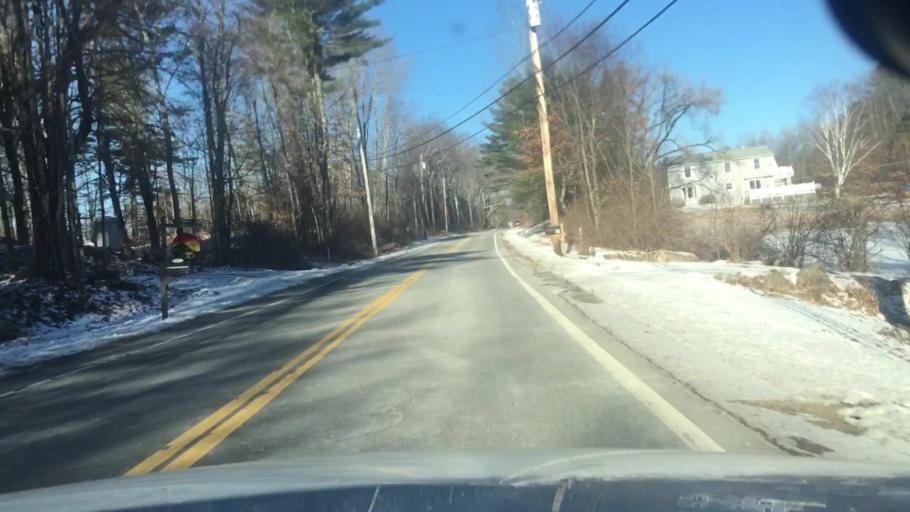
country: US
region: New Hampshire
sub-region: Merrimack County
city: Canterbury
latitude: 43.3051
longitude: -71.5670
